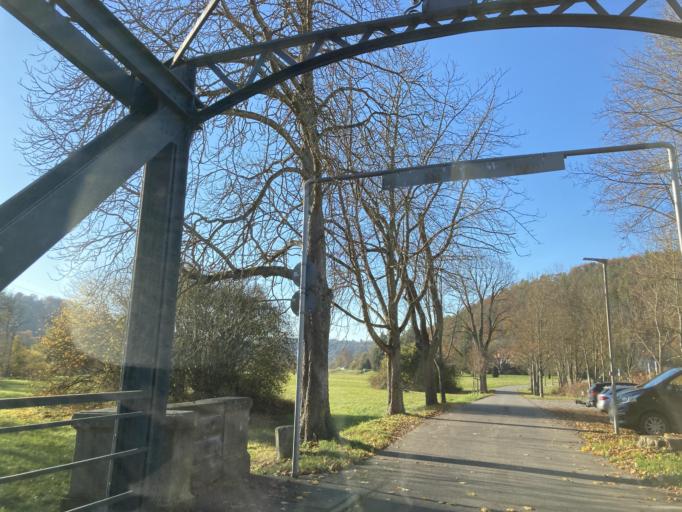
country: DE
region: Baden-Wuerttemberg
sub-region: Tuebingen Region
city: Rottenburg
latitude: 48.4590
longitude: 8.9009
